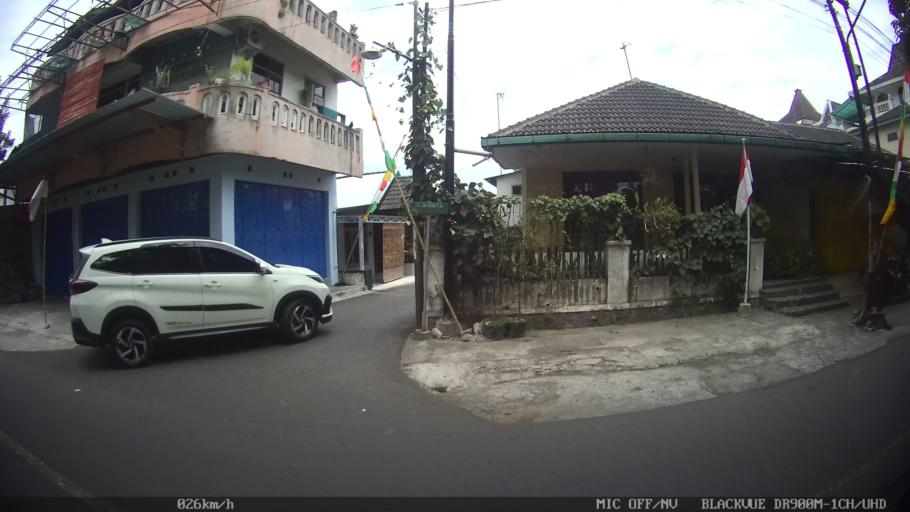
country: ID
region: Central Java
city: Candi Prambanan
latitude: -7.7562
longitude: 110.4861
